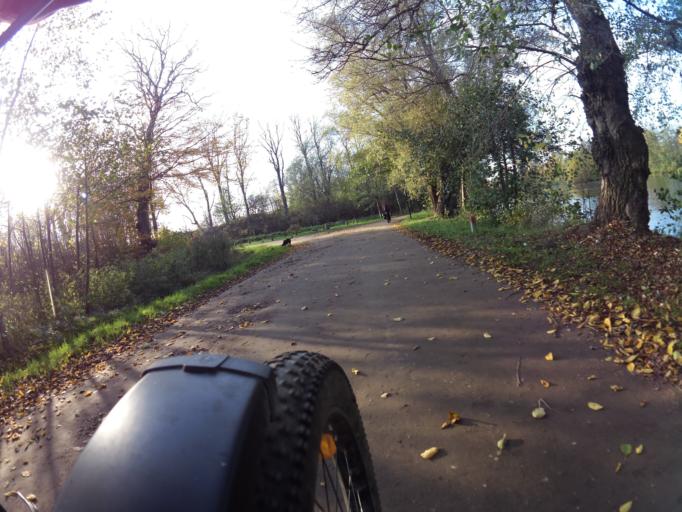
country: PL
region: Pomeranian Voivodeship
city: Strzelno
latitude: 54.7603
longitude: 18.2960
